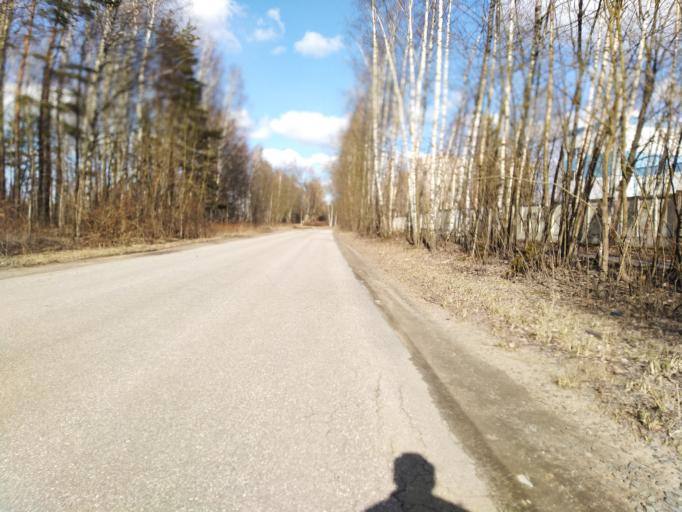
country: RU
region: Leningrad
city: Novoye Devyatkino
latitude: 60.1070
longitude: 30.4818
